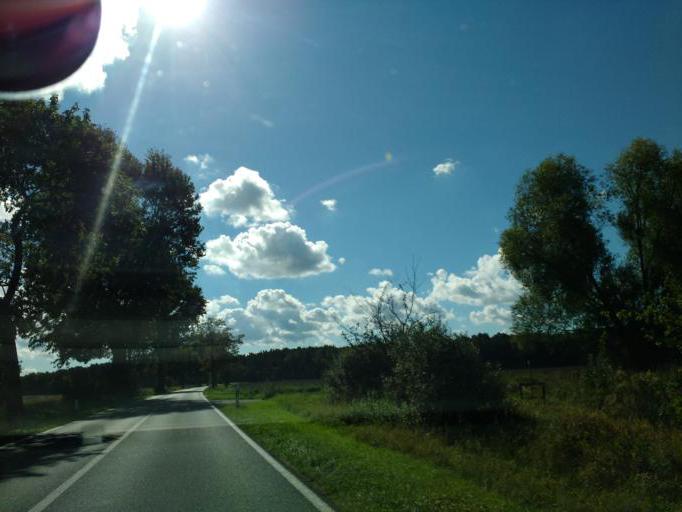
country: DE
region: Brandenburg
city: Mittenwalde
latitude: 52.2296
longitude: 13.5729
